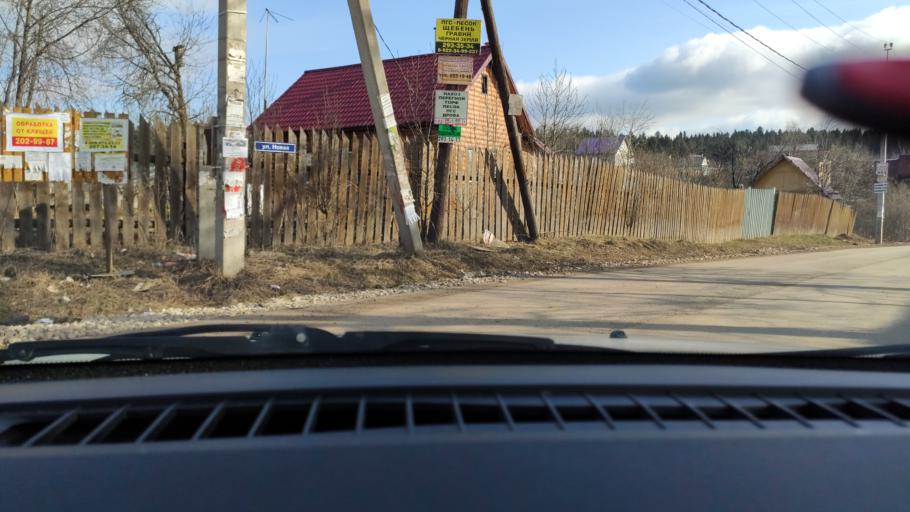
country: RU
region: Perm
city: Ferma
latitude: 57.9368
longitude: 56.3227
